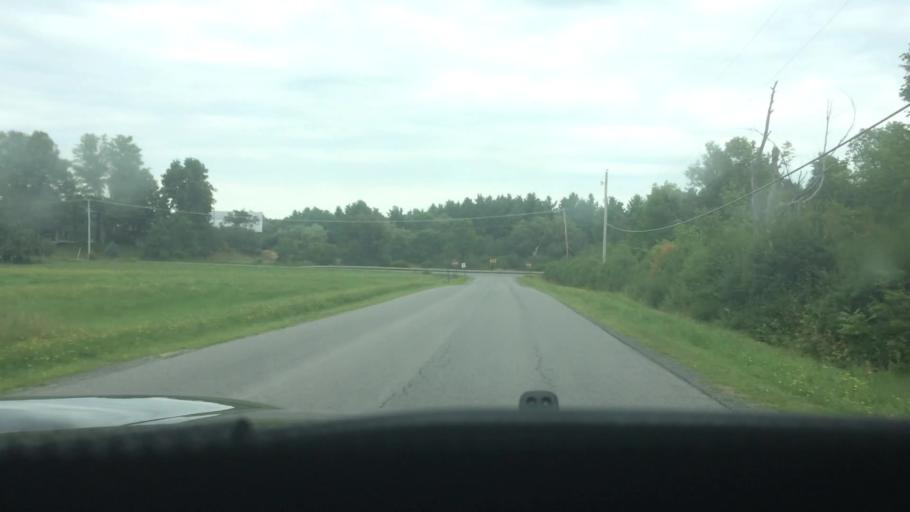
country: US
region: New York
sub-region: St. Lawrence County
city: Canton
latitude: 44.5590
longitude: -75.1211
